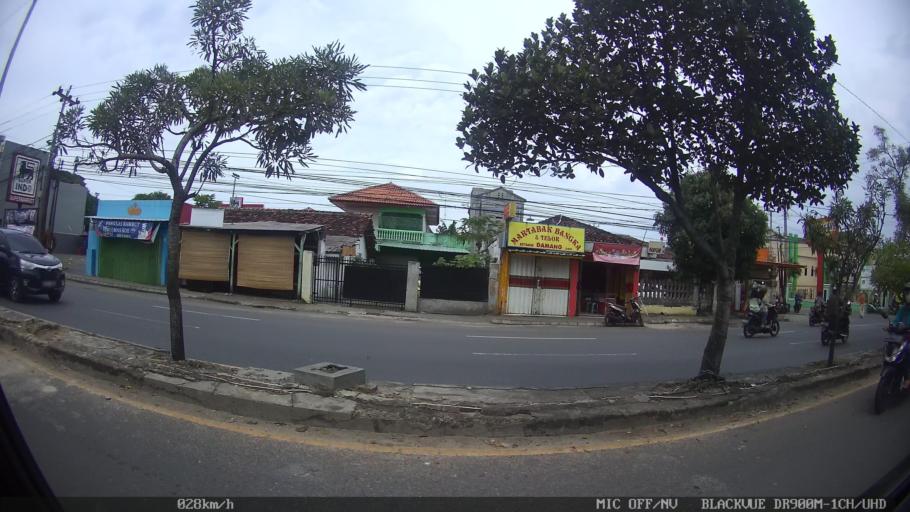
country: ID
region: Lampung
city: Kedaton
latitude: -5.3796
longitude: 105.2534
